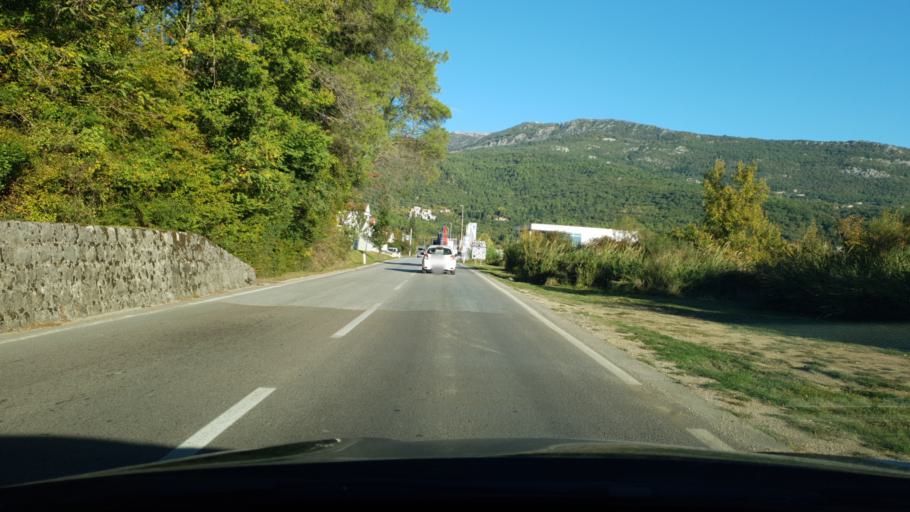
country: ME
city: Igalo
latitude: 42.4673
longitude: 18.4828
